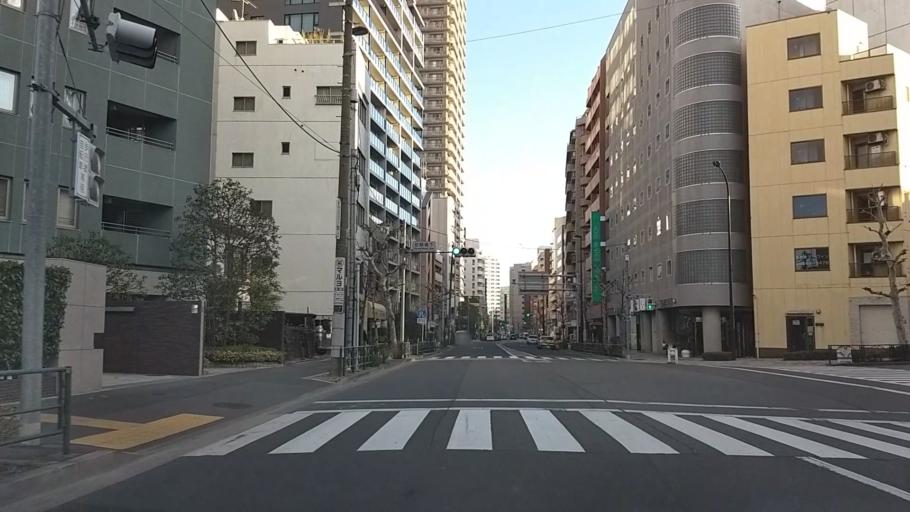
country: JP
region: Tokyo
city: Tokyo
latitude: 35.7353
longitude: 139.7268
